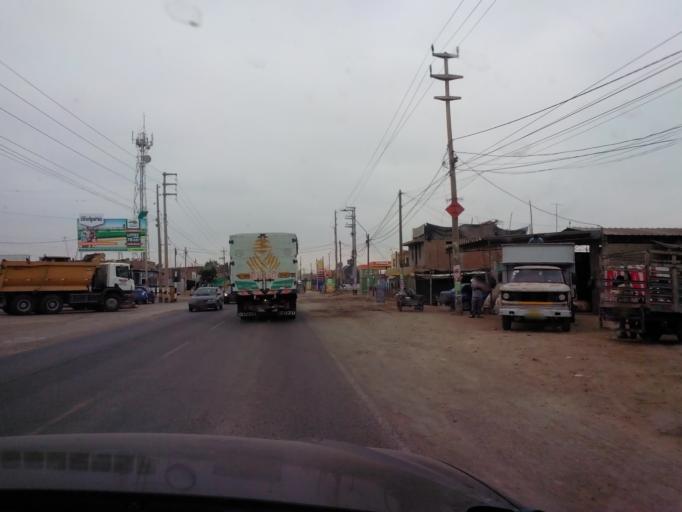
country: PE
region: Ica
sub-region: Provincia de Chincha
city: Chincha Baja
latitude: -13.4478
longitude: -76.1358
